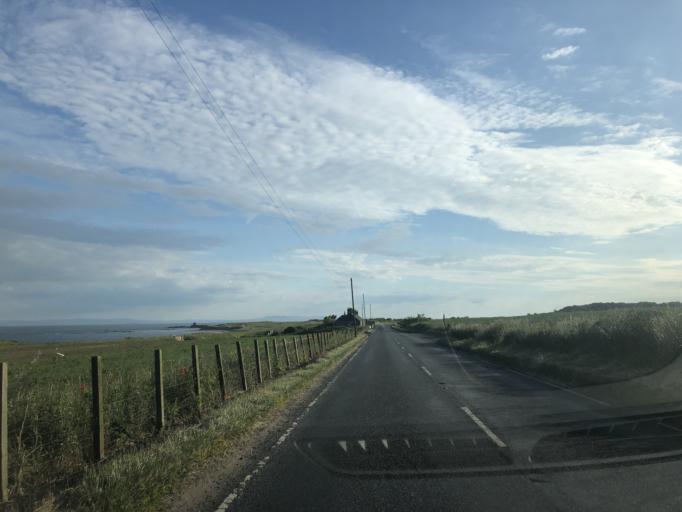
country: GB
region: Scotland
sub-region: Fife
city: Saint Monance
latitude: 56.1966
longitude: -2.7957
